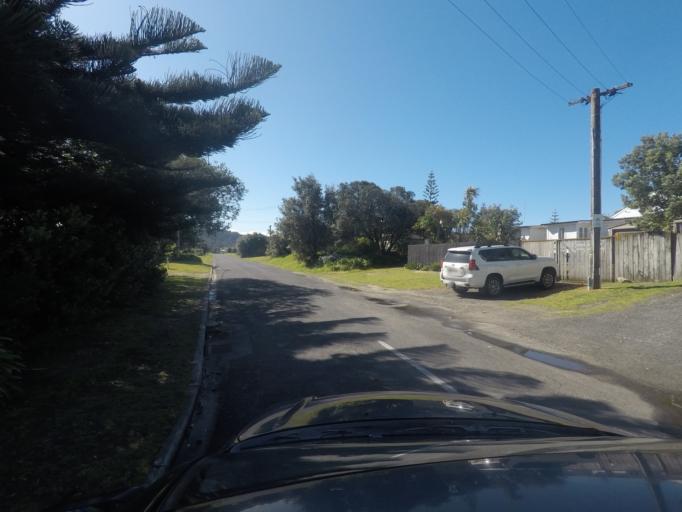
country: NZ
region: Bay of Plenty
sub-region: Western Bay of Plenty District
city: Waihi Beach
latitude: -37.4112
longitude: 175.9462
